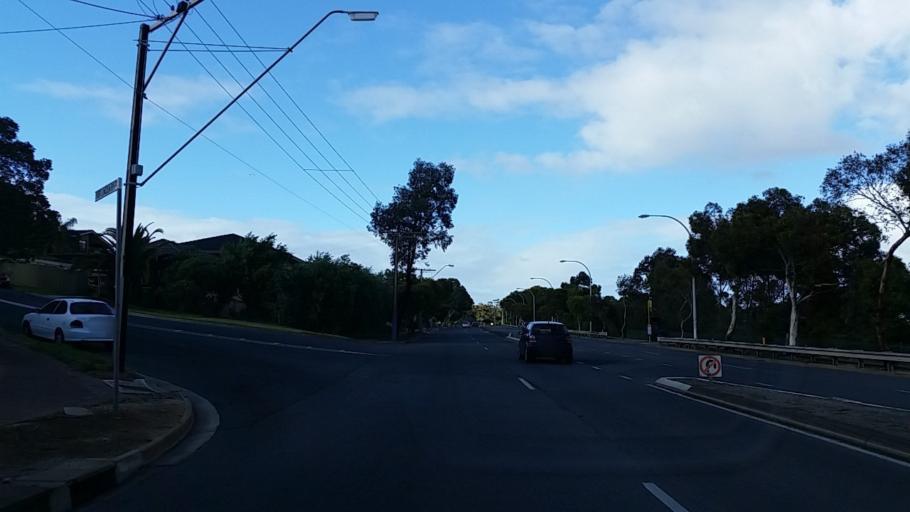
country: AU
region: South Australia
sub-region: Marion
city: Clovelly Park
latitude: -35.0068
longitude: 138.5877
